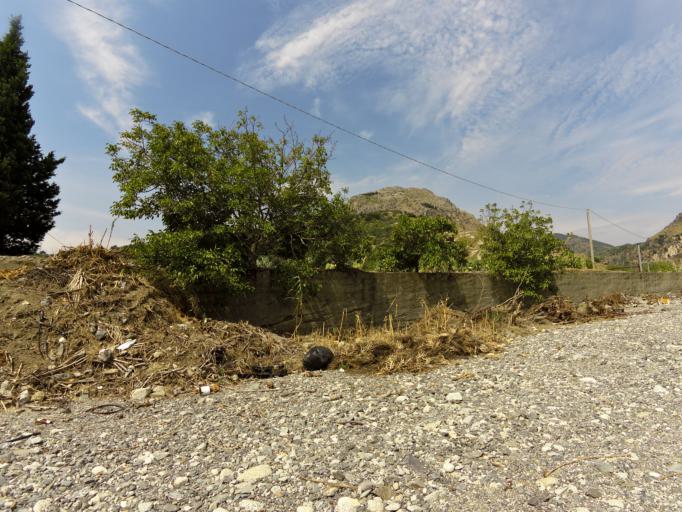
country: IT
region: Calabria
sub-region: Provincia di Reggio Calabria
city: Stilo
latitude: 38.4780
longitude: 16.4816
